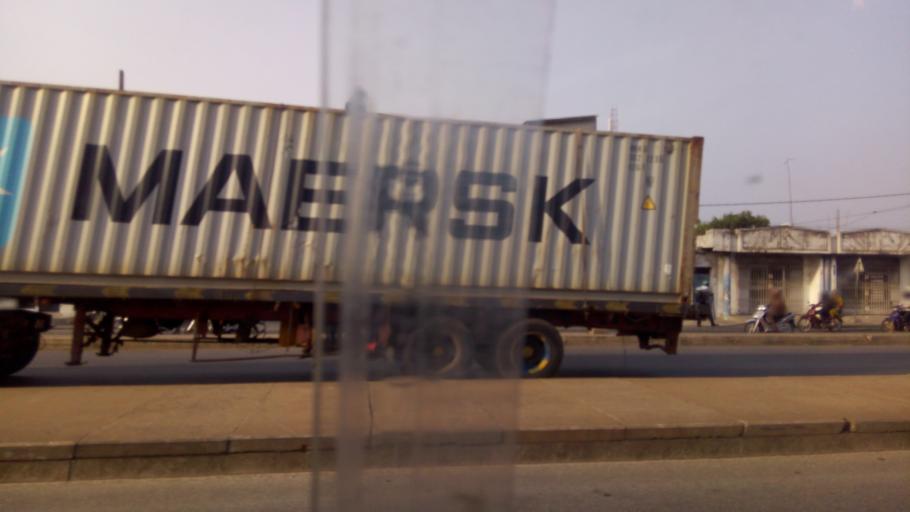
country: BJ
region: Littoral
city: Cotonou
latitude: 6.3882
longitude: 2.3653
